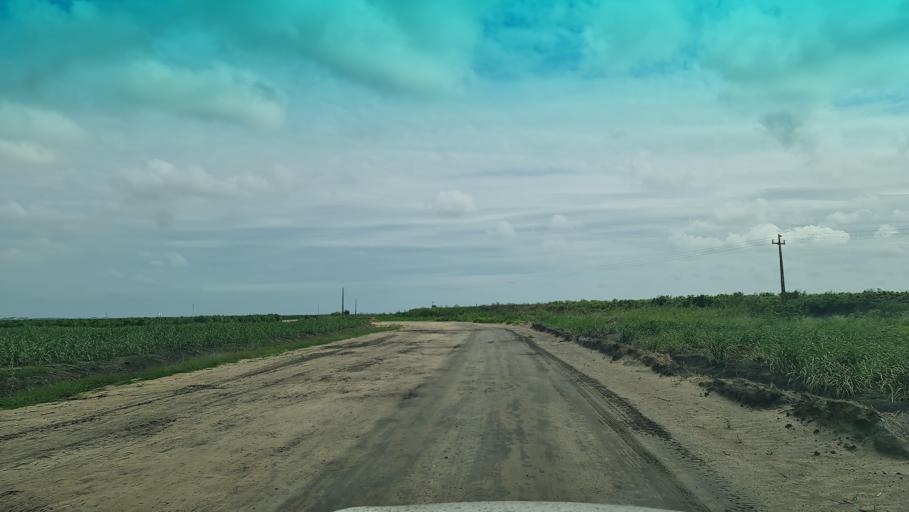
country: MZ
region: Maputo
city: Manhica
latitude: -25.4599
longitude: 32.8185
